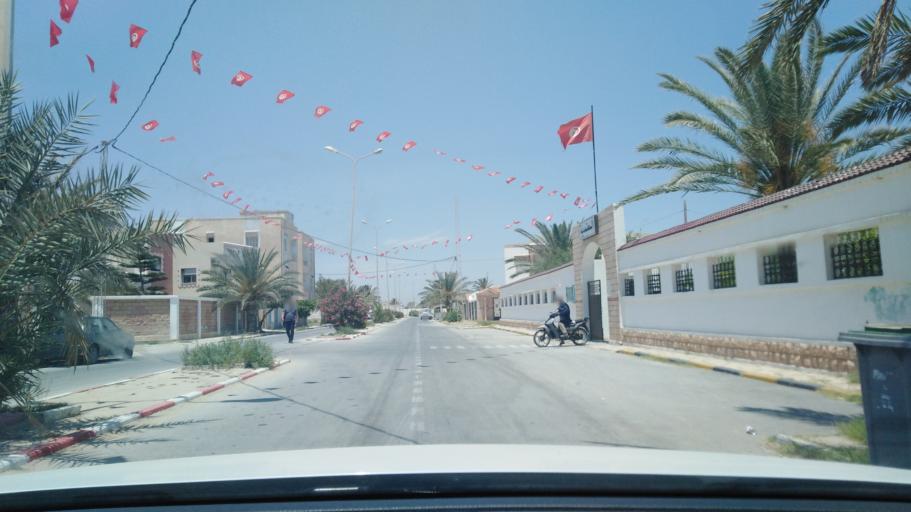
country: TN
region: Qabis
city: Gabes
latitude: 33.9476
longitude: 10.0708
